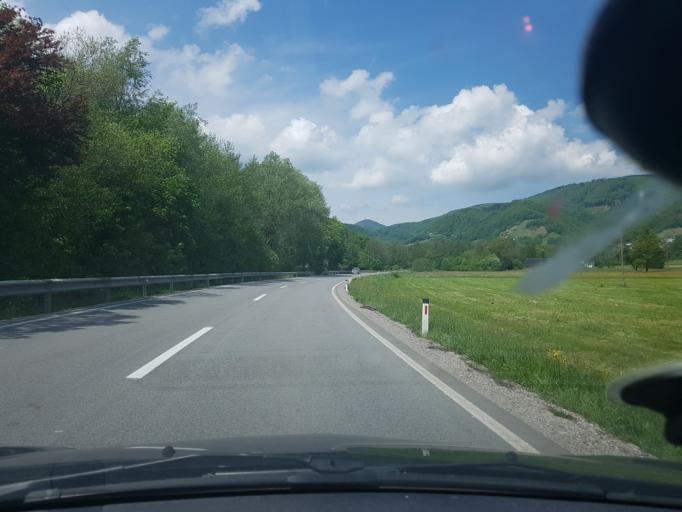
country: SI
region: Rogaska Slatina
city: Rogaska Slatina
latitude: 46.2439
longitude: 15.6541
